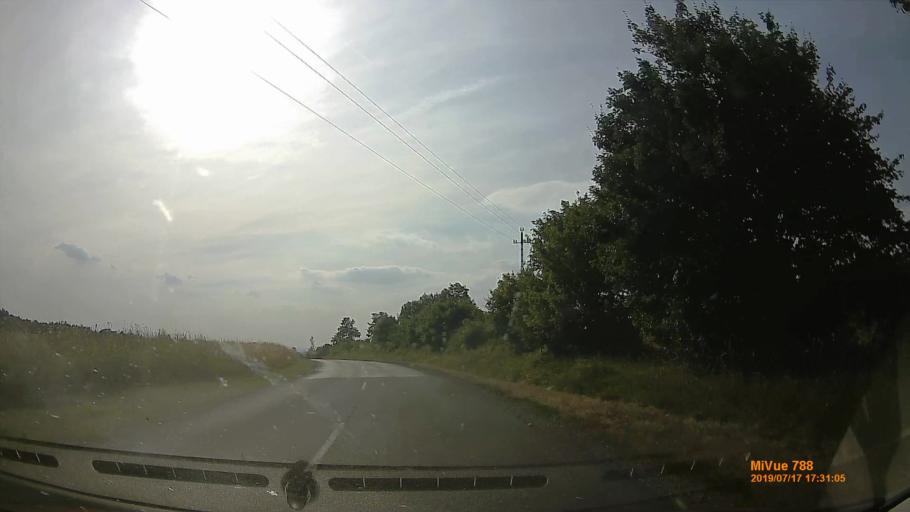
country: HU
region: Veszprem
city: Ajka
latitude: 47.0297
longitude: 17.5656
